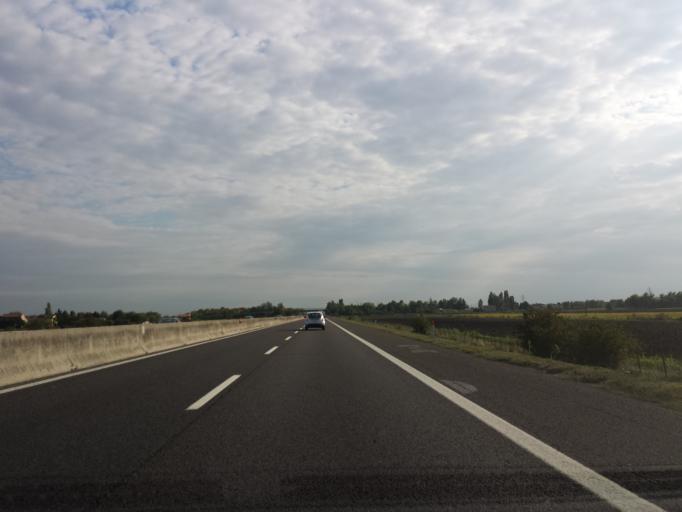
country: IT
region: Veneto
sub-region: Provincia di Padova
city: Stanghella
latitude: 45.1619
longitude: 11.7757
